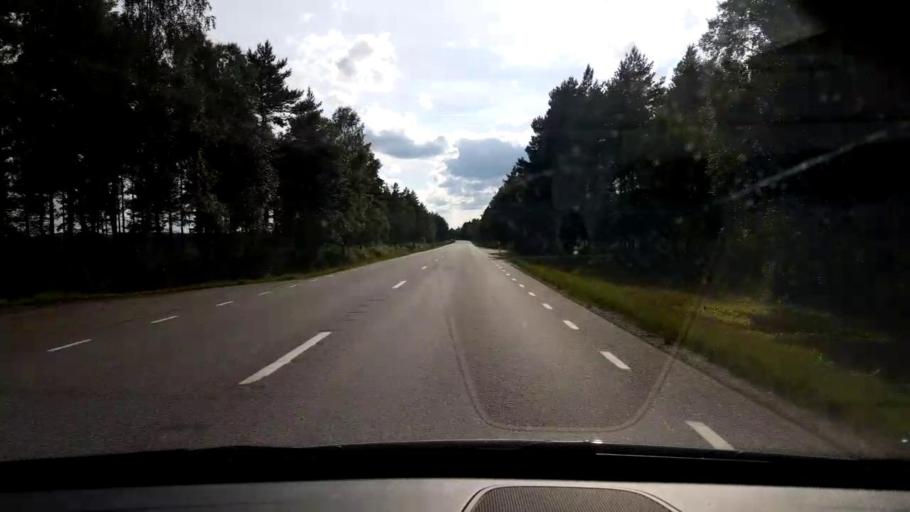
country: SE
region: Joenkoeping
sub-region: Savsjo Kommun
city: Vrigstad
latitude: 57.2883
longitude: 14.2839
